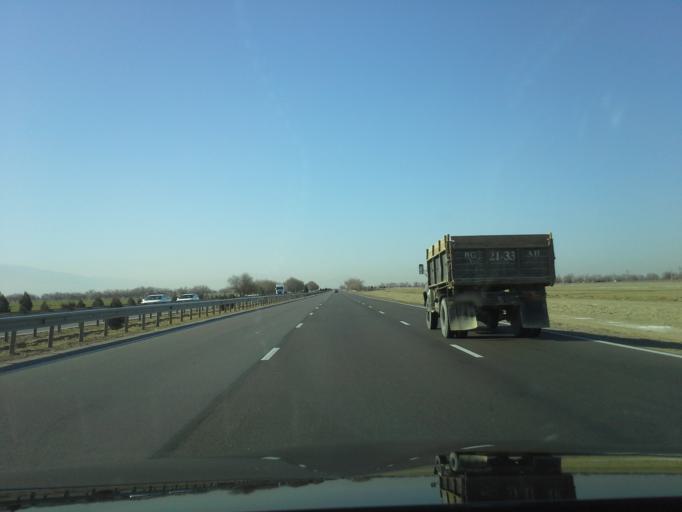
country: TM
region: Ahal
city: Annau
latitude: 37.8990
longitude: 58.5841
